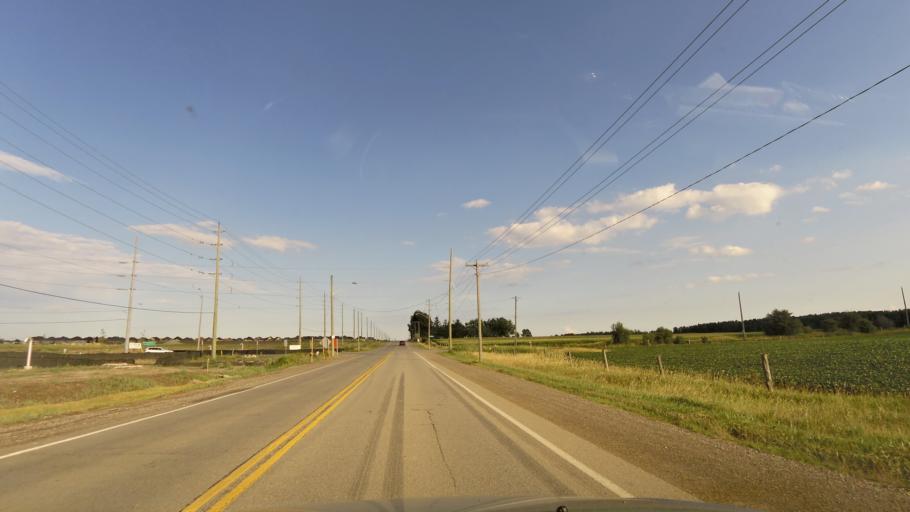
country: CA
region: Ontario
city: Brampton
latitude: 43.6873
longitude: -79.8574
